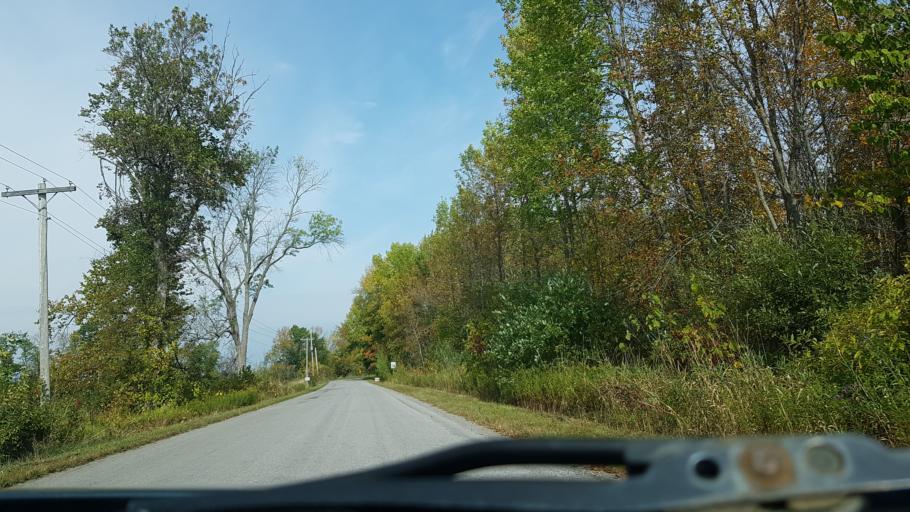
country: CA
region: Ontario
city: Orillia
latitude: 44.6434
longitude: -79.1055
